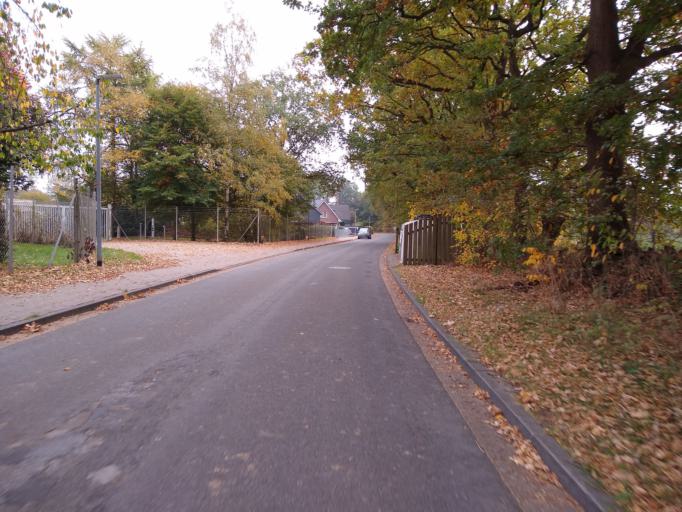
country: DE
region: Lower Saxony
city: Rastede
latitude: 53.2048
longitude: 8.2334
